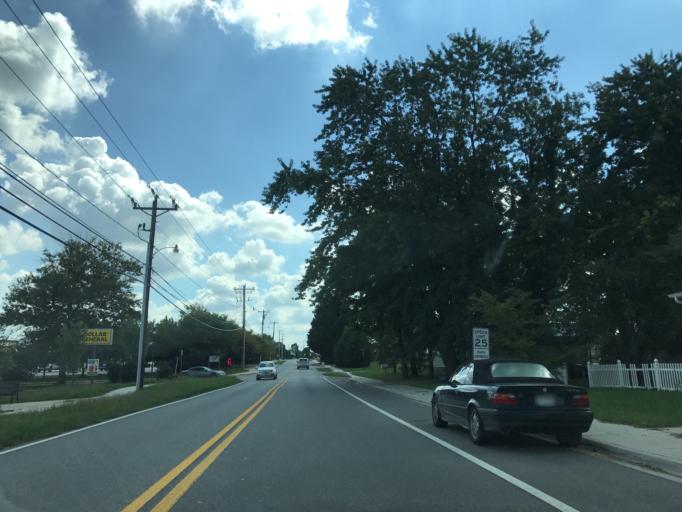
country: US
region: Maryland
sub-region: Queen Anne's County
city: Centreville
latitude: 39.0405
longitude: -76.0585
